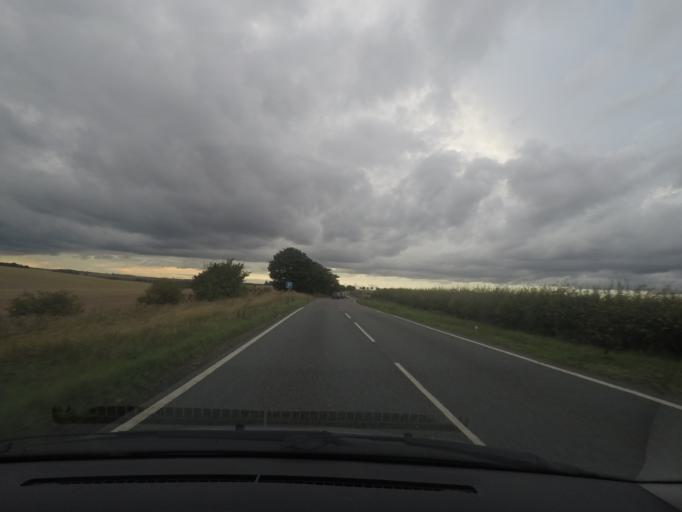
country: GB
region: England
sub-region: Lincolnshire
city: Burwell
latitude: 53.3063
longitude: 0.0221
